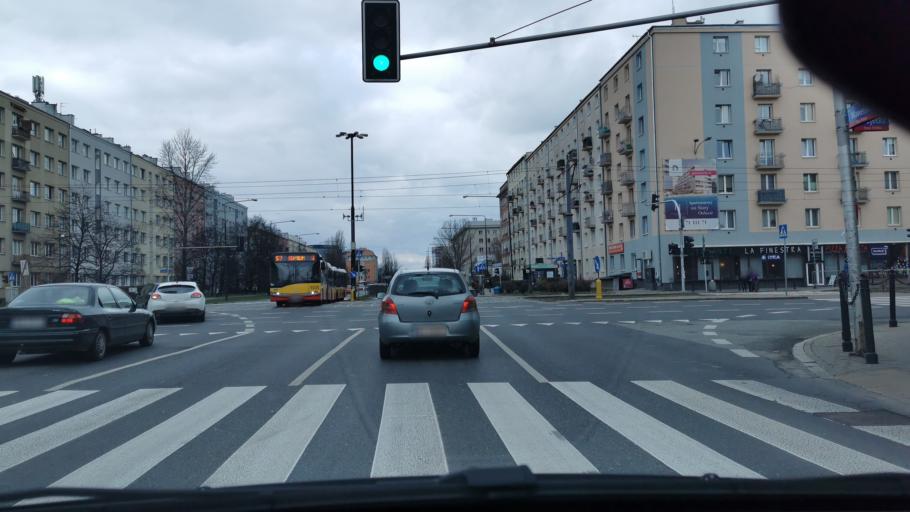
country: PL
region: Masovian Voivodeship
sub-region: Warszawa
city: Ochota
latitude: 52.2162
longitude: 20.9817
